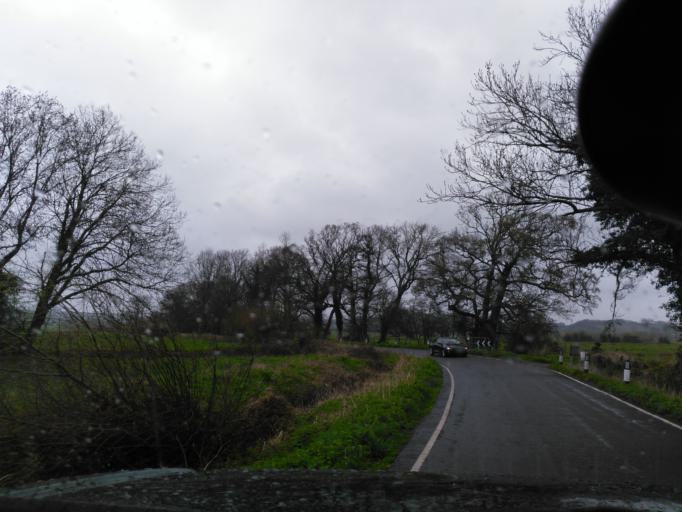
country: GB
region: England
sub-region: Somerset
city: Langport
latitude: 51.1025
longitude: -2.8177
